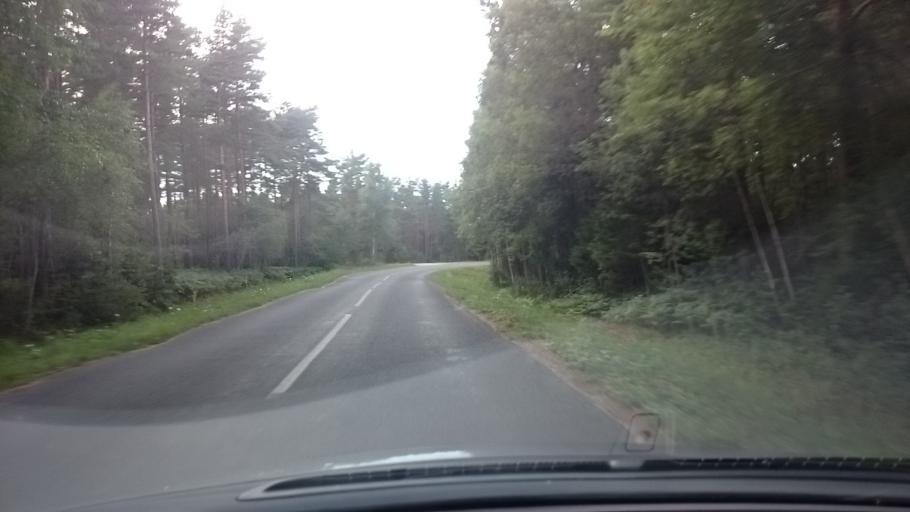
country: EE
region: Saare
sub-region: Kuressaare linn
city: Kuressaare
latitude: 58.4175
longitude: 22.0766
